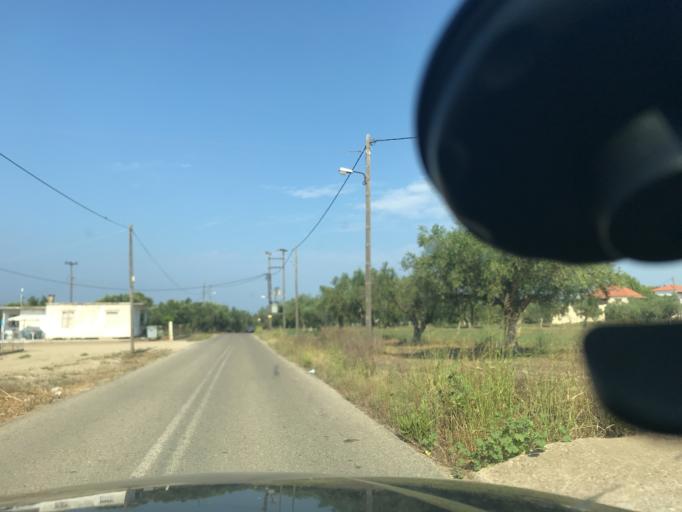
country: GR
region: West Greece
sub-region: Nomos Ileias
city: Kardamas
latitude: 37.7185
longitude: 21.3266
